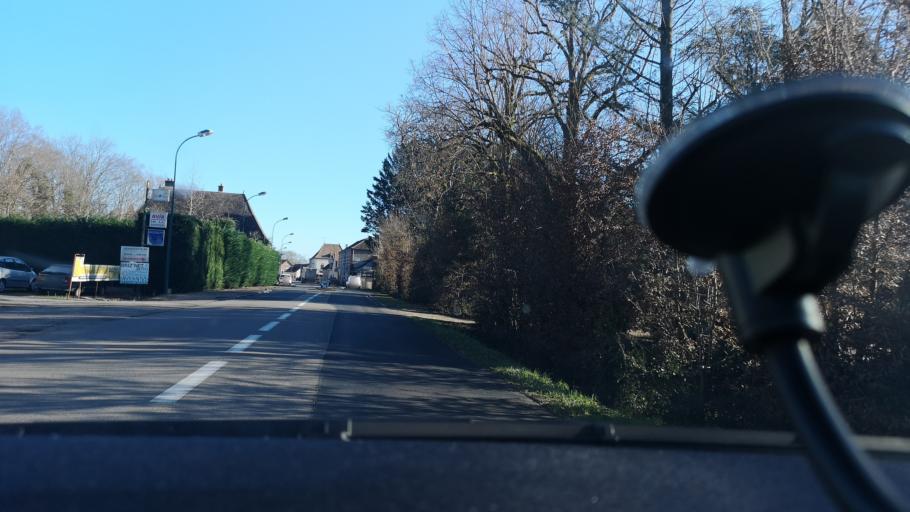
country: FR
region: Bourgogne
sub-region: Departement de Saone-et-Loire
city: Saint-Martin-en-Bresse
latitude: 46.7411
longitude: 5.0904
